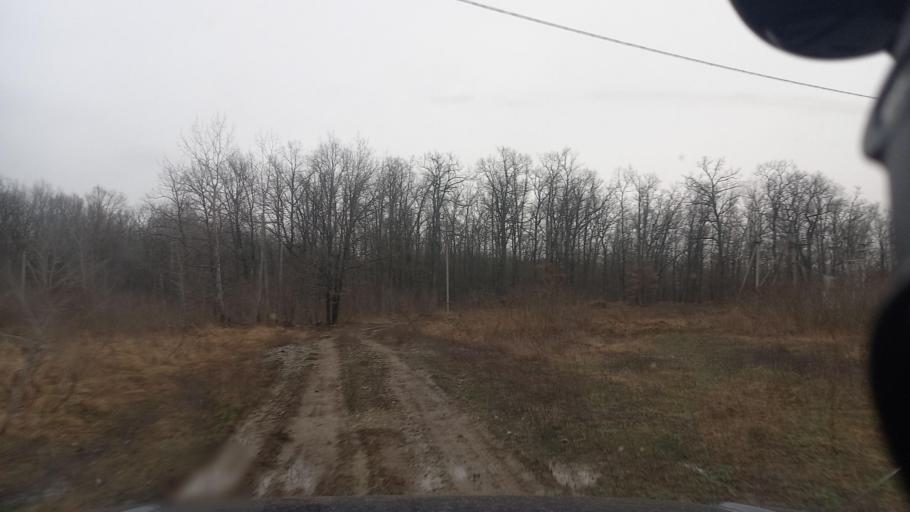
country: RU
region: Krasnodarskiy
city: Saratovskaya
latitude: 44.6604
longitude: 39.2260
